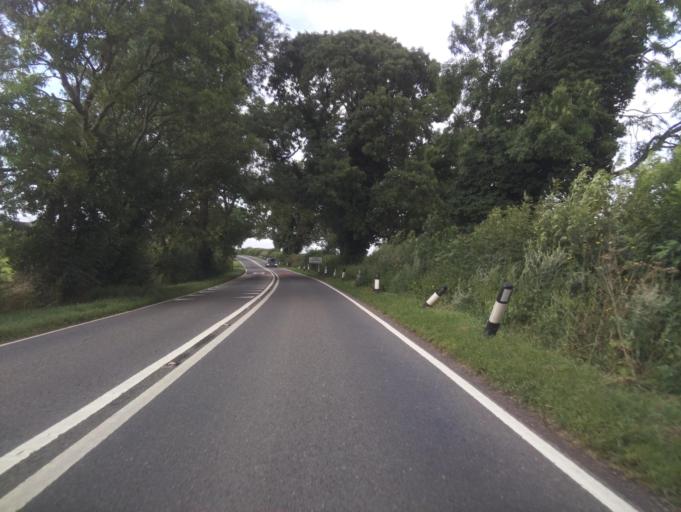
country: GB
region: England
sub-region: Warwickshire
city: Dunchurch
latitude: 52.3052
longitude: -1.3123
